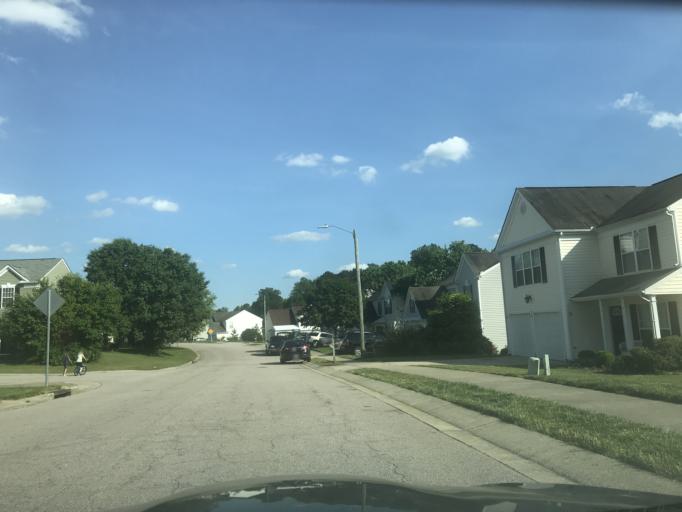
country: US
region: North Carolina
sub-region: Wake County
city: Knightdale
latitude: 35.8444
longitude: -78.5517
